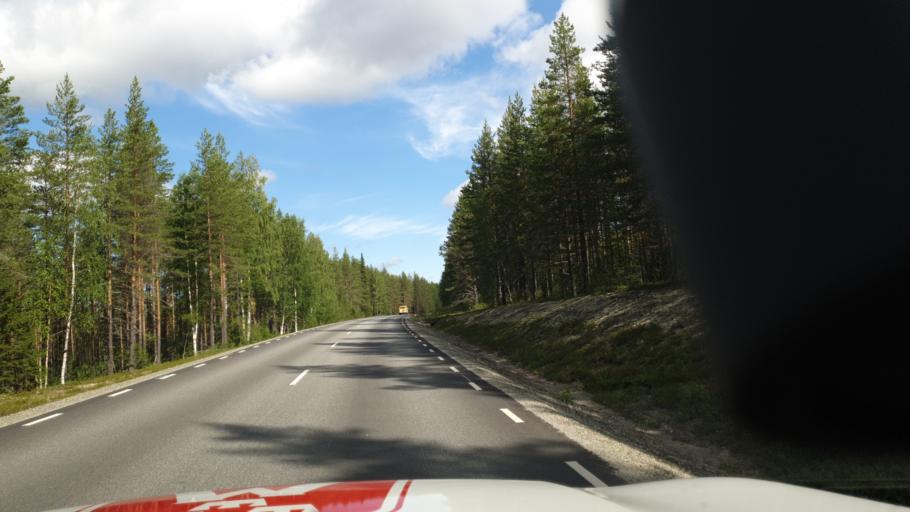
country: SE
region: Vaesterbotten
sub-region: Norsjo Kommun
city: Norsjoe
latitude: 64.6124
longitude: 19.2921
